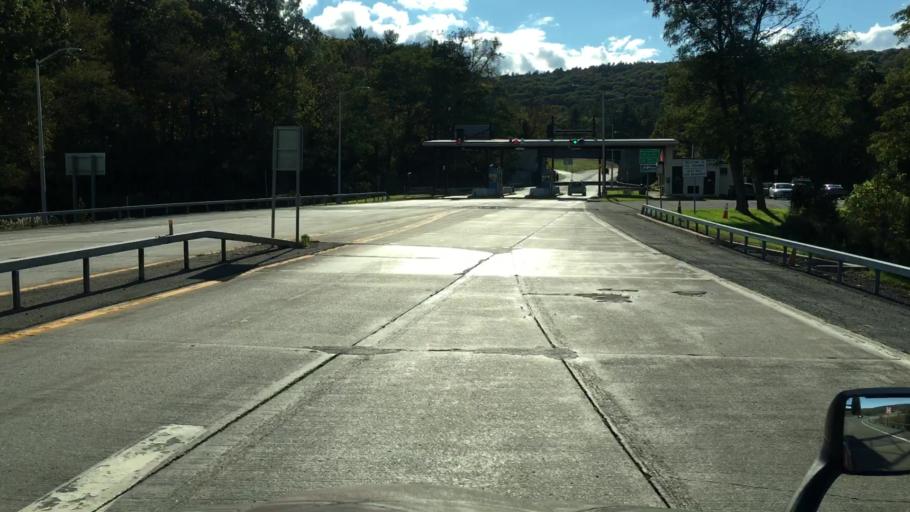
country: US
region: New York
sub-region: Schenectady County
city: Scotia
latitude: 42.8406
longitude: -74.0065
